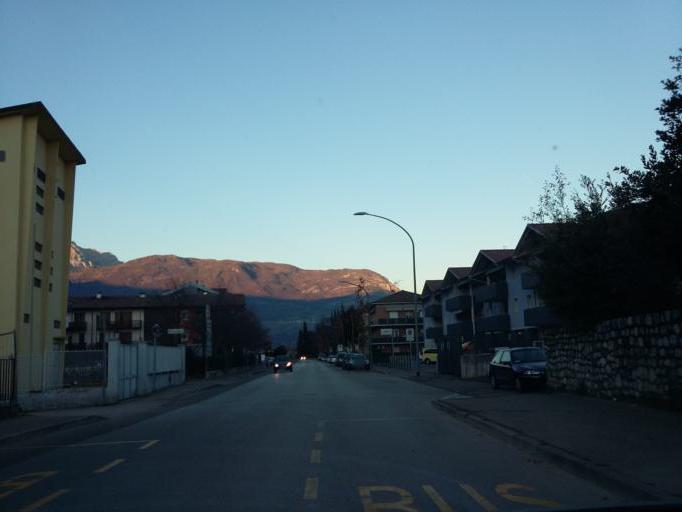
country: IT
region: Trentino-Alto Adige
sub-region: Provincia di Trento
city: Rovereto
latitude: 45.8936
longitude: 11.0275
